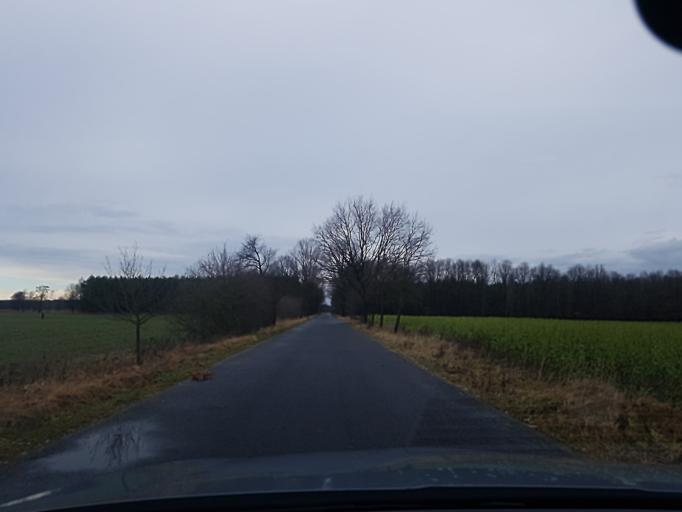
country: DE
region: Brandenburg
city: Falkenberg
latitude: 51.6018
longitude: 13.2913
